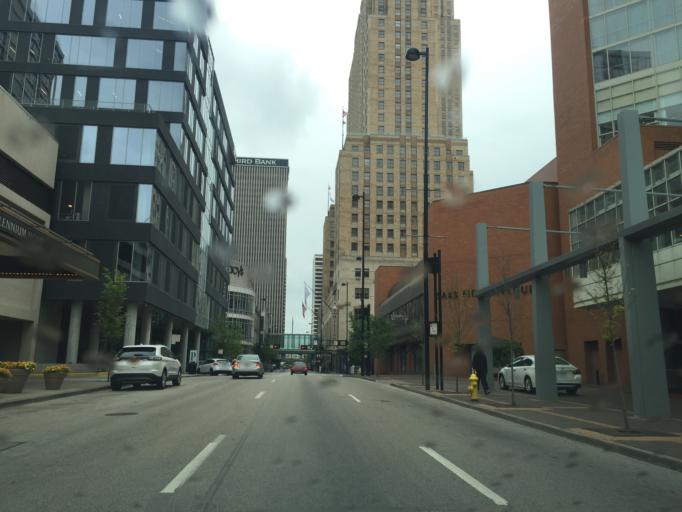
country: US
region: Kentucky
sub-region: Kenton County
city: Covington
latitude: 39.1007
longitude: -84.5159
